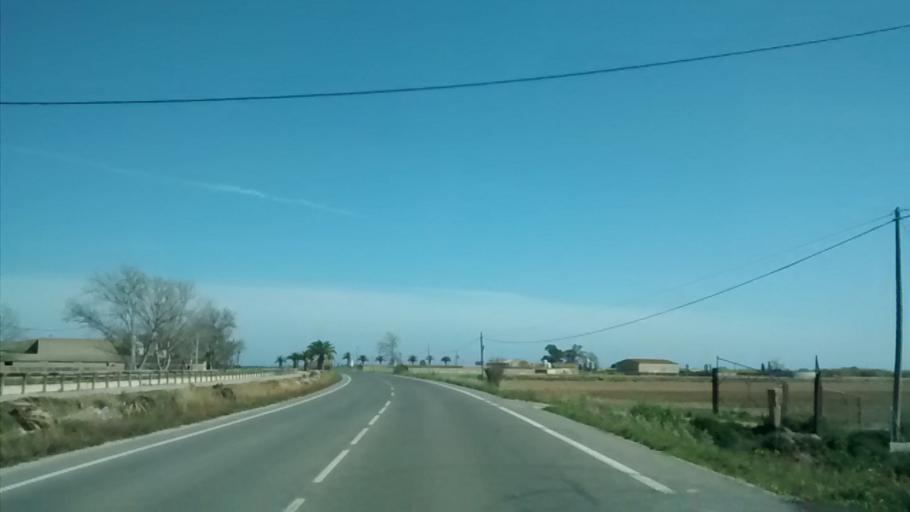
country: ES
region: Catalonia
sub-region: Provincia de Tarragona
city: Deltebre
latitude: 40.7088
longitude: 0.7603
